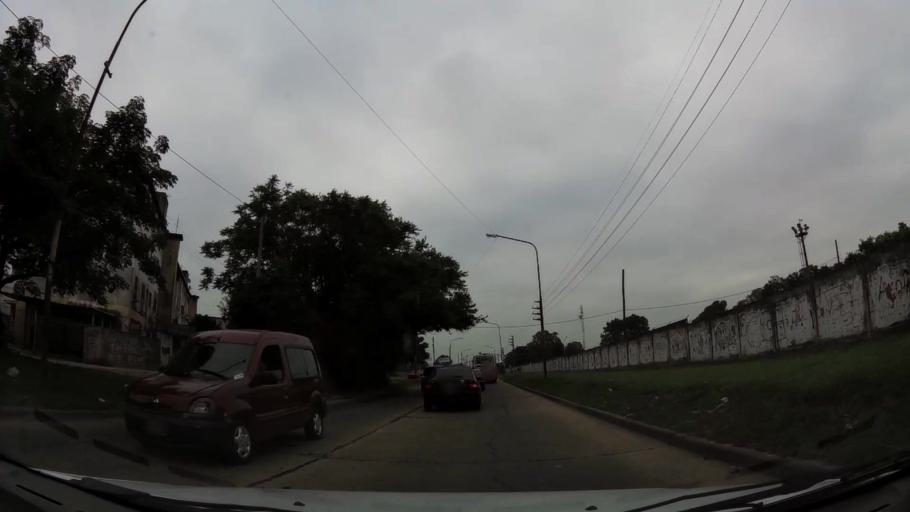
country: AR
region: Buenos Aires
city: San Justo
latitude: -34.7022
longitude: -58.5441
